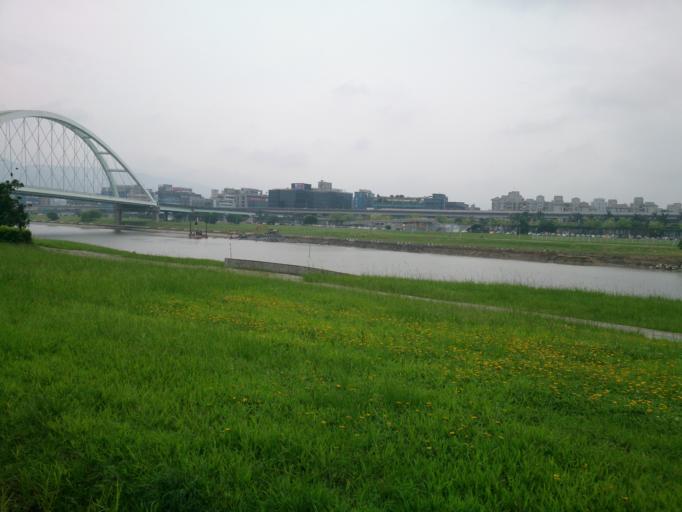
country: TW
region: Taipei
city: Taipei
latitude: 25.0533
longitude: 121.5706
